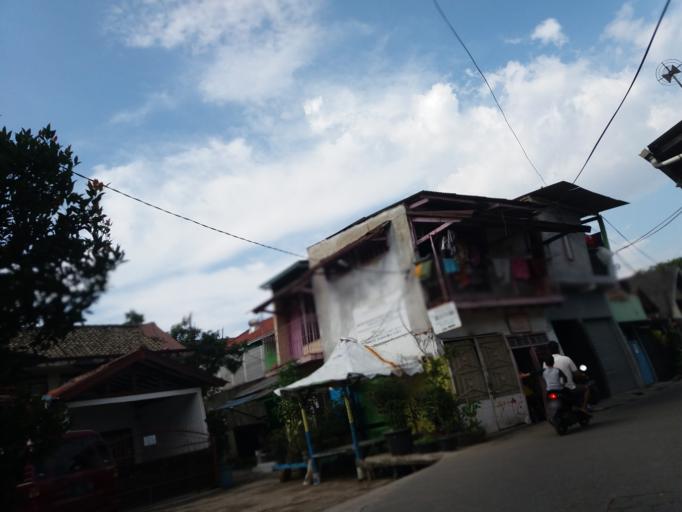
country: ID
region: West Java
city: Bandung
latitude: -6.9240
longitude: 107.6465
